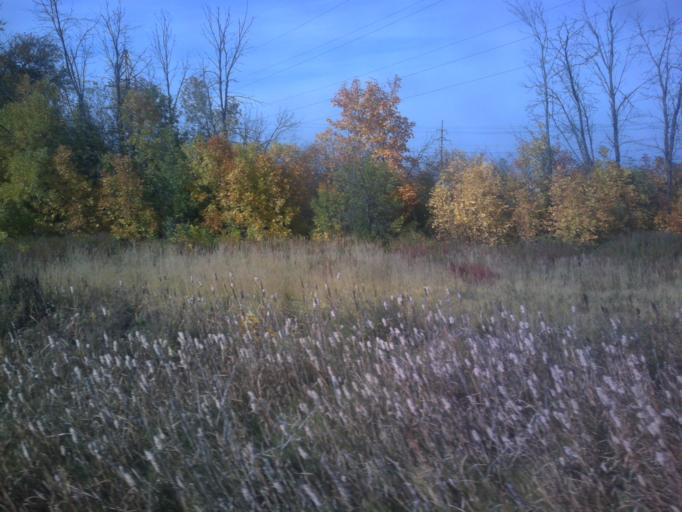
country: RU
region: Moskovskaya
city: Shcherbinka
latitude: 55.4872
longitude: 37.5553
